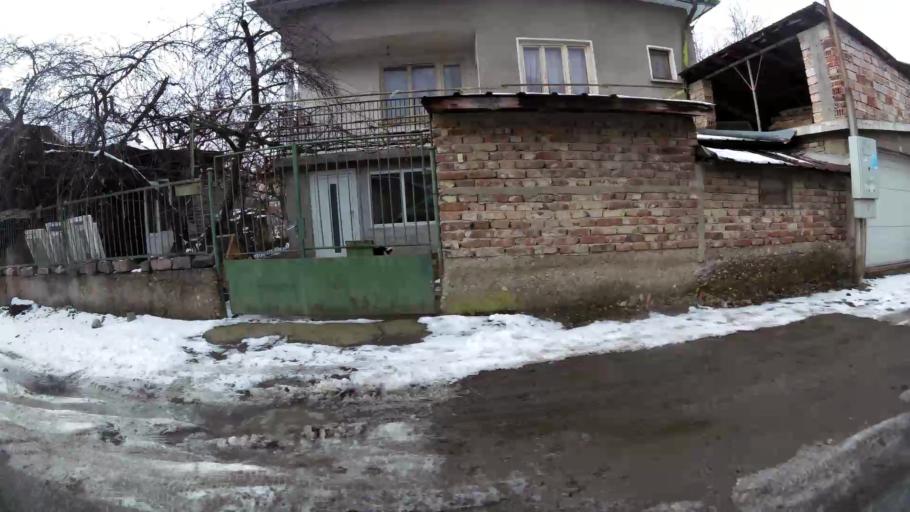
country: BG
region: Sofia-Capital
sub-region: Stolichna Obshtina
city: Sofia
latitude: 42.7146
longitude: 23.4146
